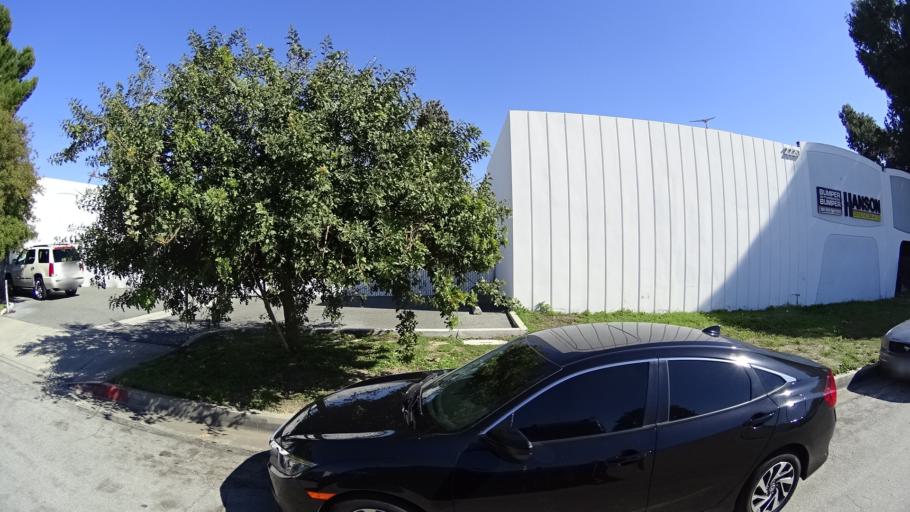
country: US
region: California
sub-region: Orange County
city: Orange
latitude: 33.7945
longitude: -117.8844
